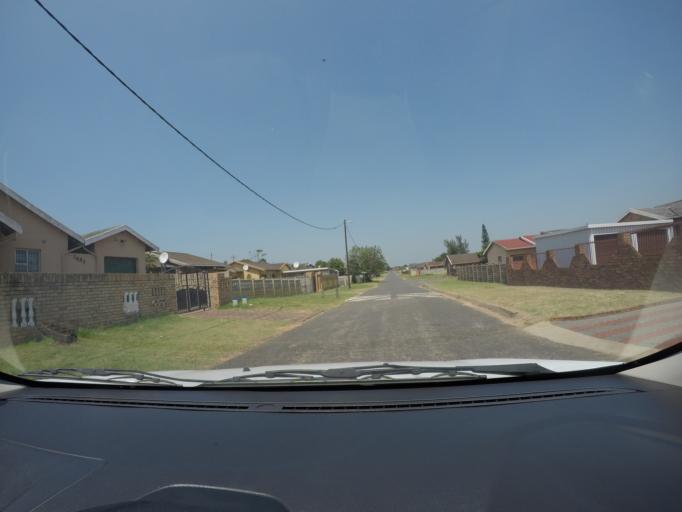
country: ZA
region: KwaZulu-Natal
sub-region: uThungulu District Municipality
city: eSikhawini
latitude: -28.8705
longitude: 31.9241
